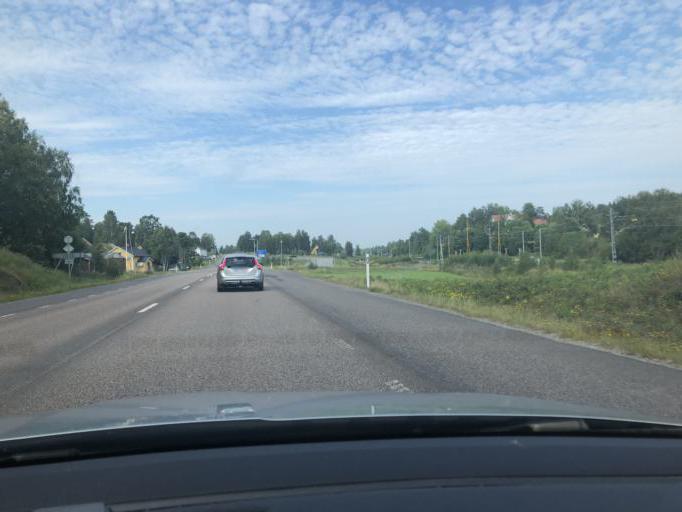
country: SE
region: Vaesternorrland
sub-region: Kramfors Kommun
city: Kramfors
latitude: 62.9021
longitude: 17.8339
